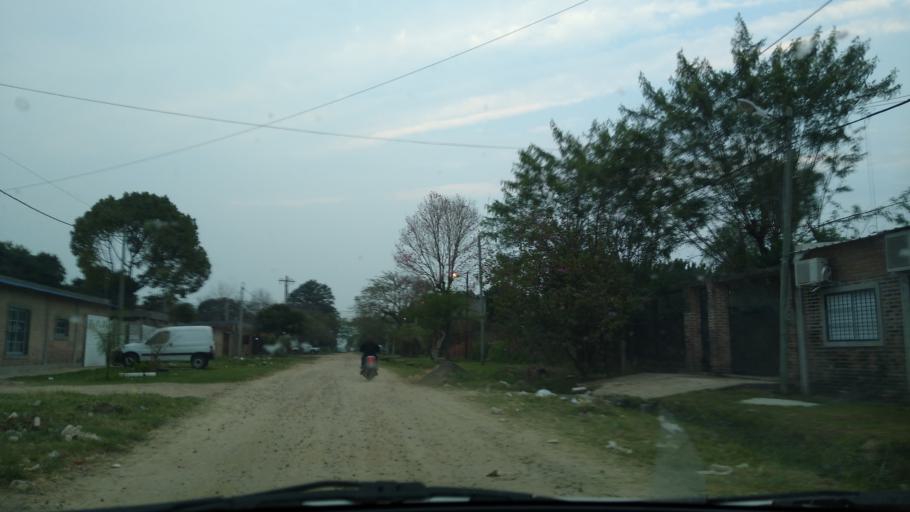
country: AR
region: Chaco
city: Barranqueras
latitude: -27.4872
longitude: -58.9514
